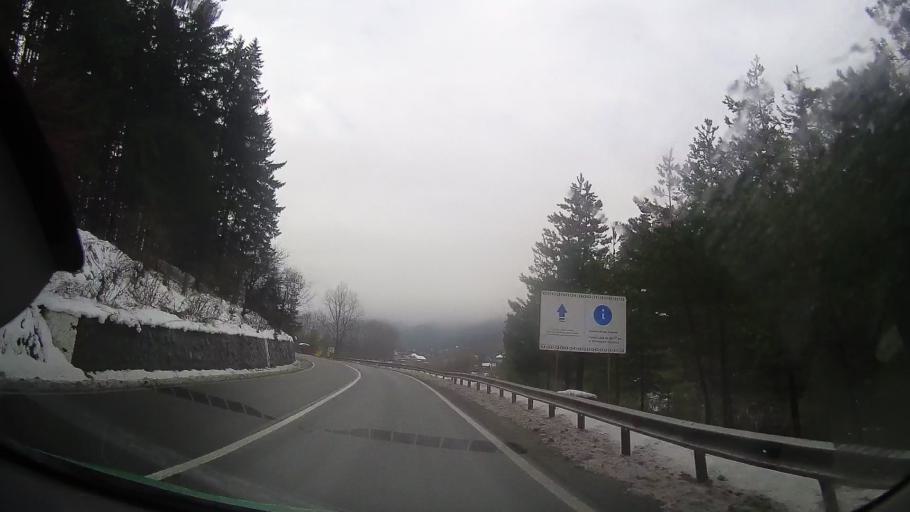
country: RO
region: Neamt
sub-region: Comuna Tasca
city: Tasca
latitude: 46.8968
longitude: 26.0444
